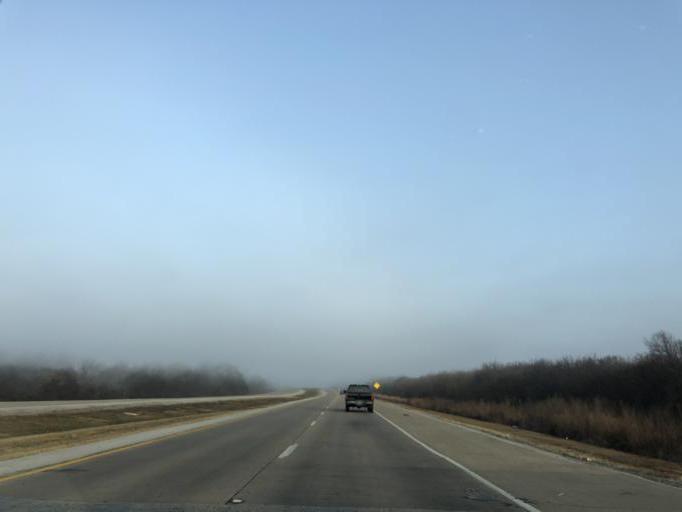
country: US
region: Texas
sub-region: Dallas County
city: Duncanville
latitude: 32.6584
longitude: -96.9805
